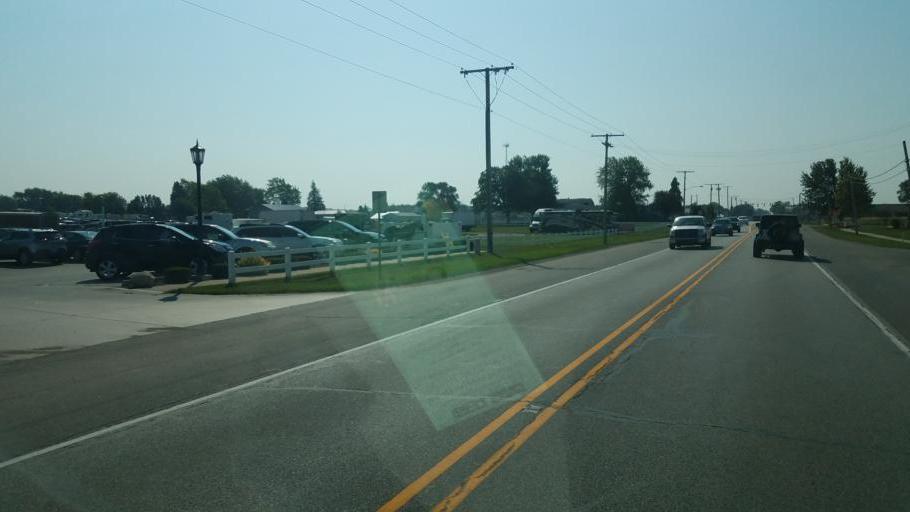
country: US
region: Indiana
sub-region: Elkhart County
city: Middlebury
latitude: 41.6717
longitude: -85.5806
